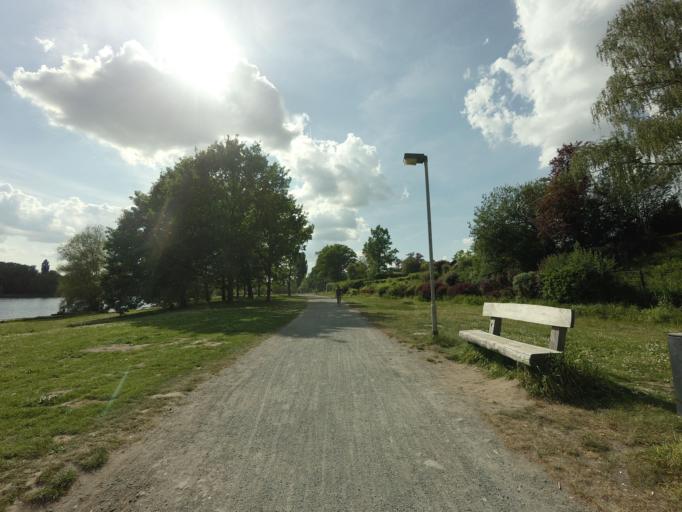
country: DE
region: Lower Saxony
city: Braunschweig
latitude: 52.2890
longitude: 10.5123
